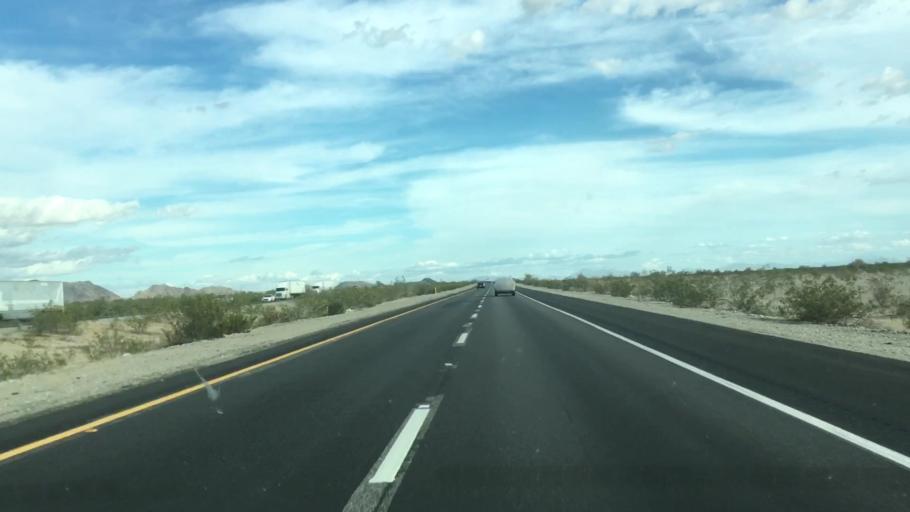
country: US
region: California
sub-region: Riverside County
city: Mesa Verde
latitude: 33.6096
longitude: -114.8378
